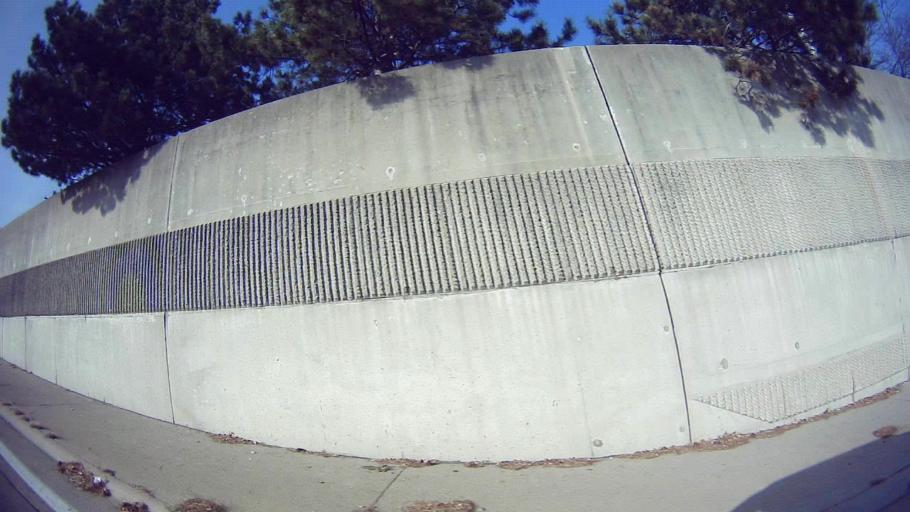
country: US
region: Michigan
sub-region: Oakland County
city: Southfield
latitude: 42.4774
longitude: -83.1990
